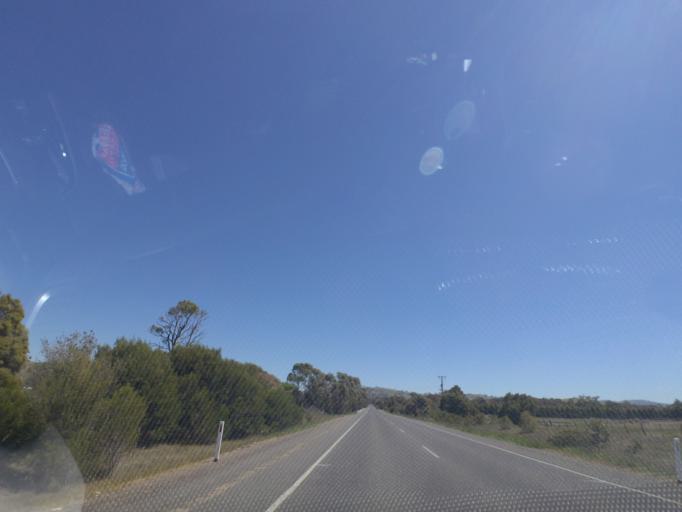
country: AU
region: Victoria
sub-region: Hume
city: Sunbury
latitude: -37.3060
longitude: 144.8369
